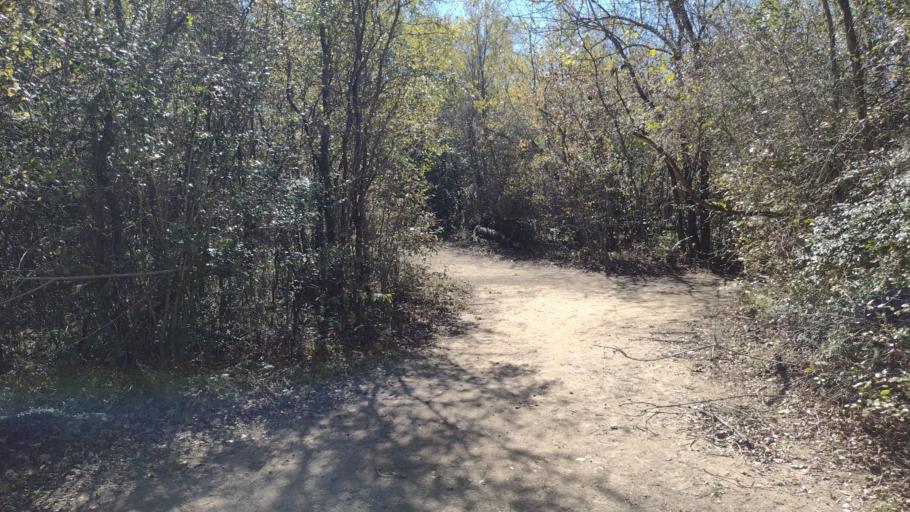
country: US
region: Texas
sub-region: Dallas County
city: Farmers Branch
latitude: 32.9159
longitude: -96.9372
